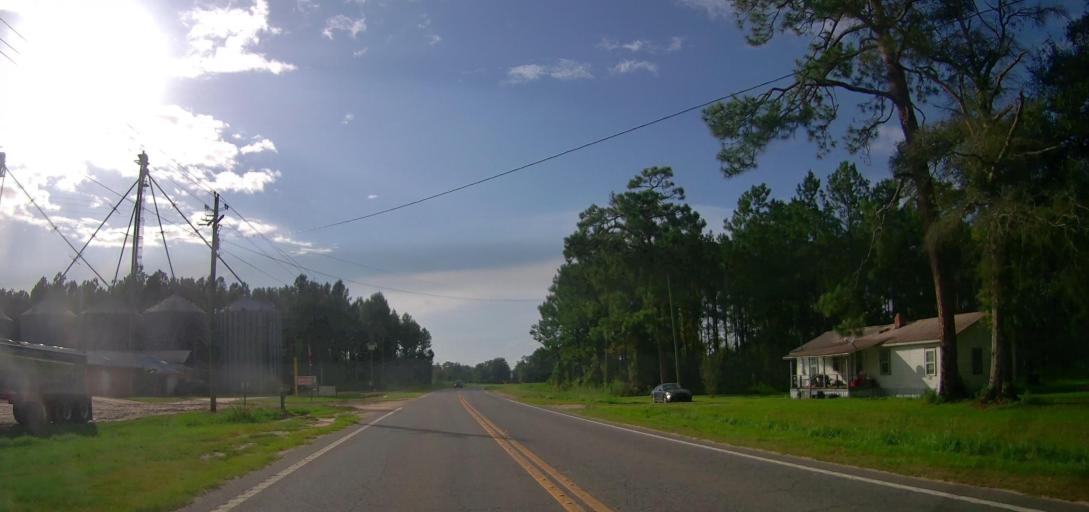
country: US
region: Georgia
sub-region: Coffee County
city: Nicholls
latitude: 31.3417
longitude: -82.6061
